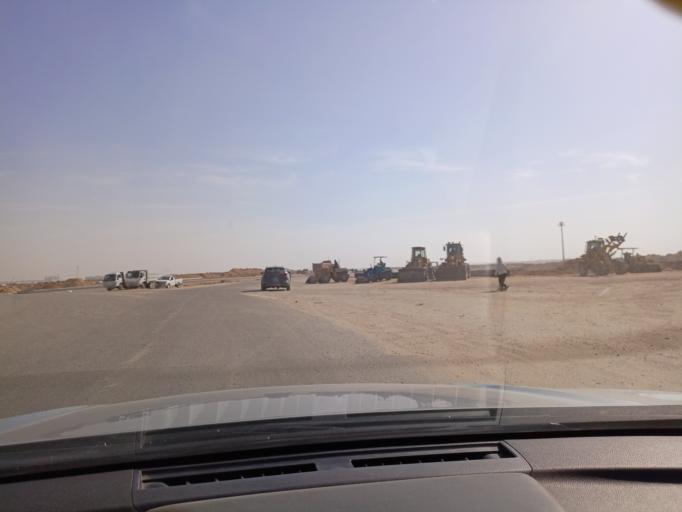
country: EG
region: Muhafazat al Qalyubiyah
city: Al Khankah
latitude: 30.0240
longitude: 31.6766
